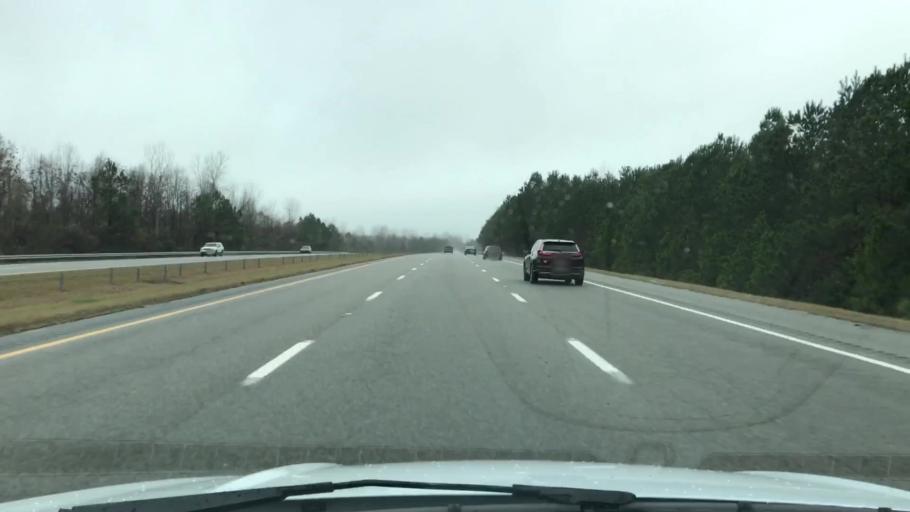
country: US
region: South Carolina
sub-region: Horry County
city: Myrtle Beach
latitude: 33.7498
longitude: -78.8745
